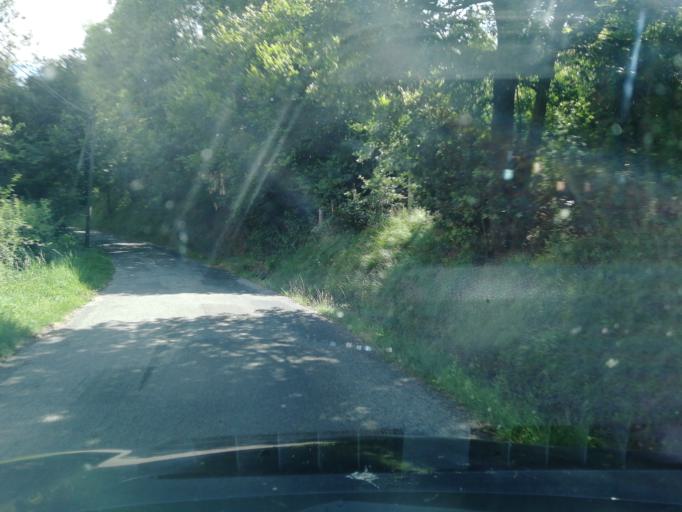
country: FR
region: Rhone-Alpes
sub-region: Departement du Rhone
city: Saint-Didier-sous-Riverie
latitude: 45.6336
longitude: 4.6259
